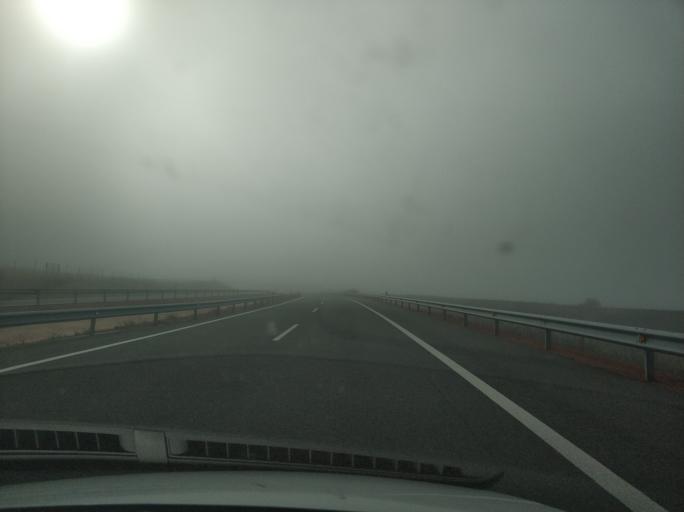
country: ES
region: Castille and Leon
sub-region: Provincia de Soria
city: Yelo
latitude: 41.2386
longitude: -2.4797
